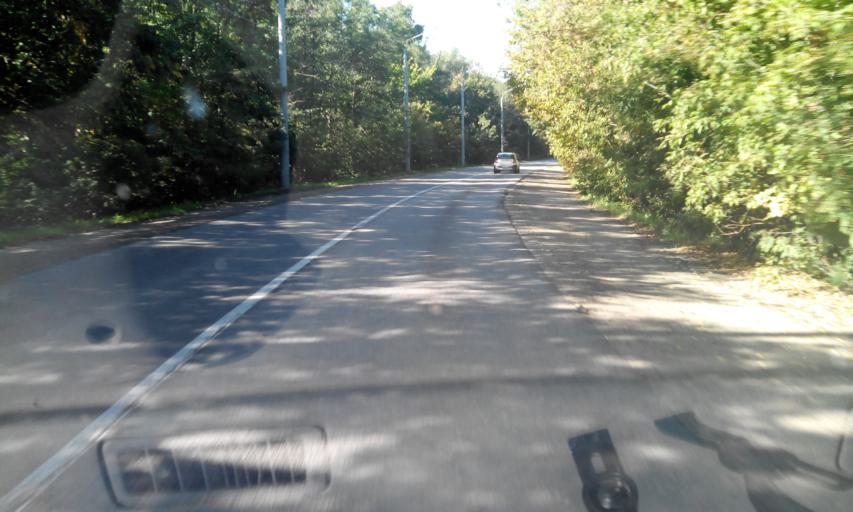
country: RU
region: Penza
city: Penza
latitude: 53.2115
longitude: 45.0832
